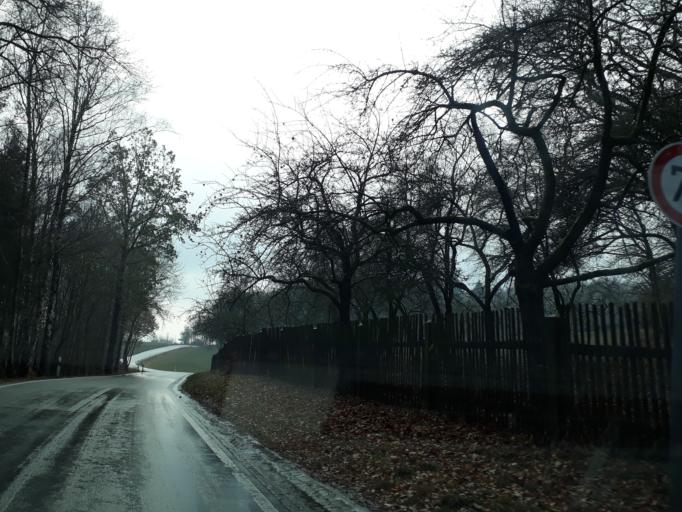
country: DE
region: Saxony
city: Eibau
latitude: 51.0043
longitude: 14.6723
